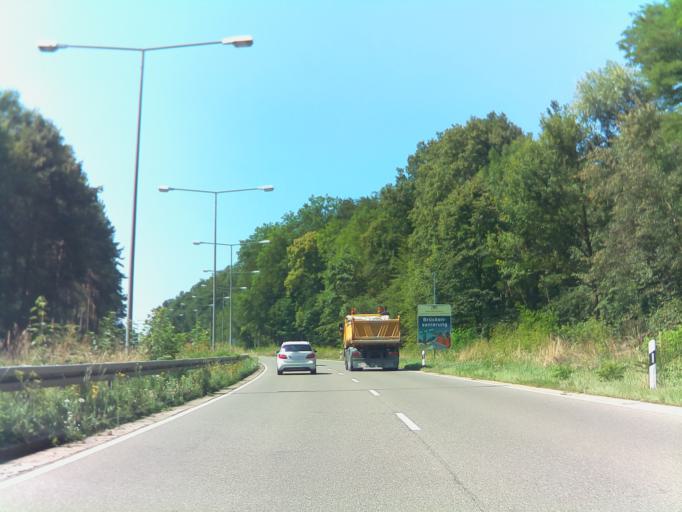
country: DE
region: Baden-Wuerttemberg
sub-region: Regierungsbezirk Stuttgart
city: Gerlingen
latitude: 48.7829
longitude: 9.0810
